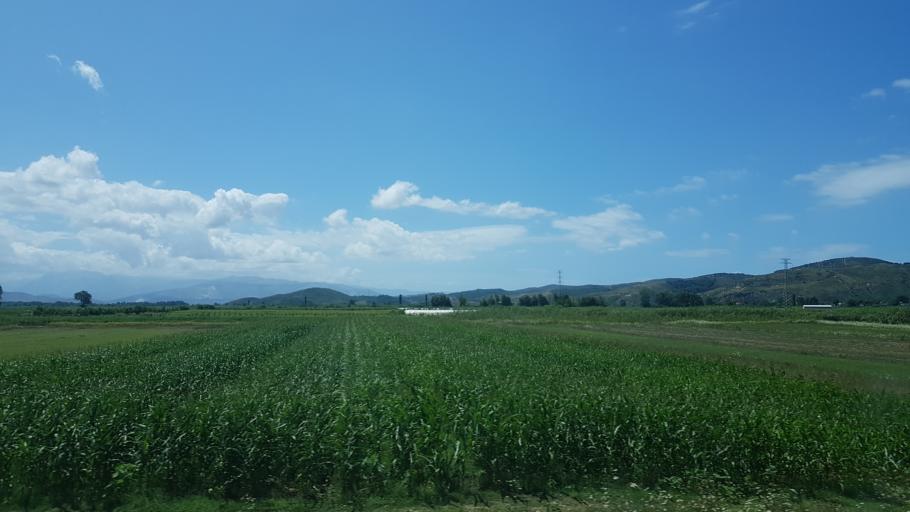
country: AL
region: Fier
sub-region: Rrethi i Fierit
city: Frakulla e Madhe
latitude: 40.6043
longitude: 19.5509
